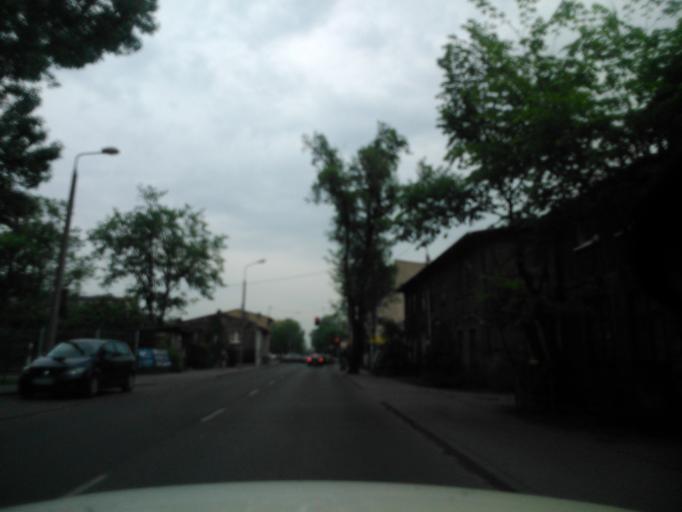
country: PL
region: Kujawsko-Pomorskie
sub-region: Torun
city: Torun
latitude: 53.0234
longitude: 18.6226
